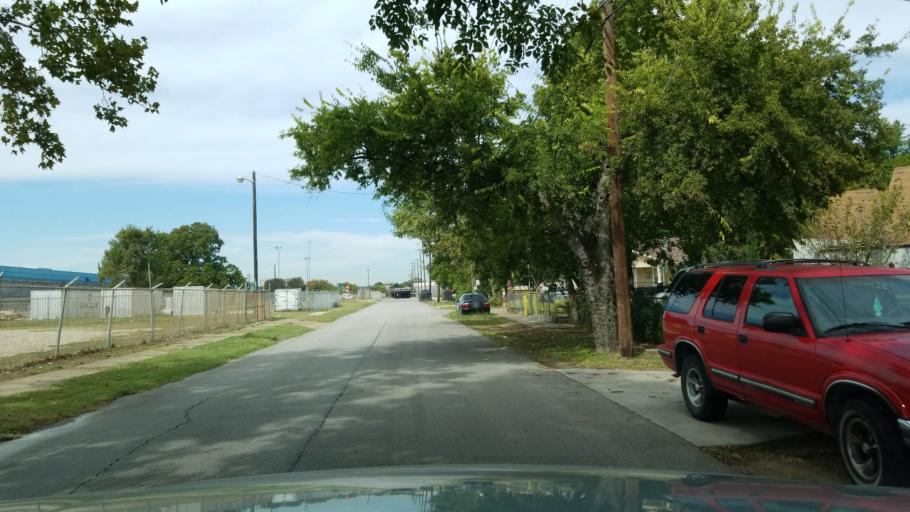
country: US
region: Texas
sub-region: Dallas County
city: Dallas
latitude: 32.7877
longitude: -96.7463
